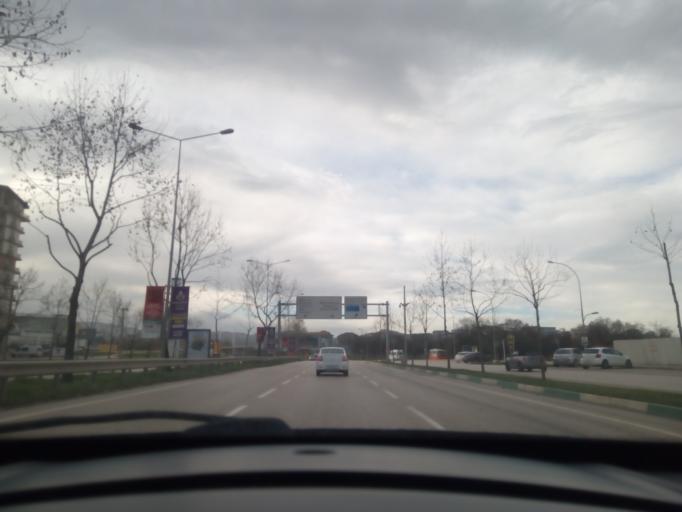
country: TR
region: Bursa
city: Cali
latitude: 40.2165
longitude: 28.9521
